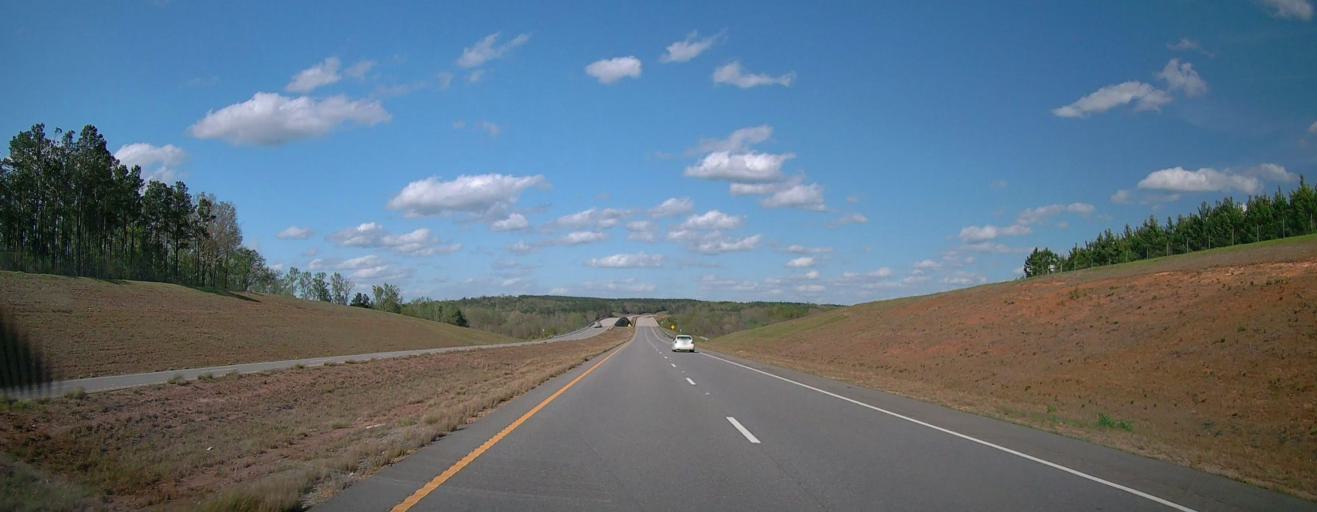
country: US
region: Georgia
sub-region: Baldwin County
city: Hardwick
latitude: 33.0200
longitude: -83.1897
